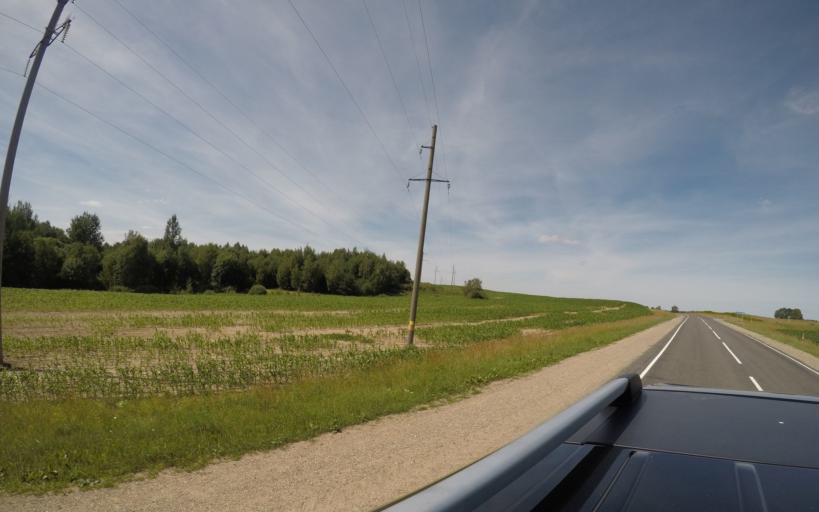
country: BY
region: Grodnenskaya
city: Hal'shany
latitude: 54.2685
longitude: 25.9899
